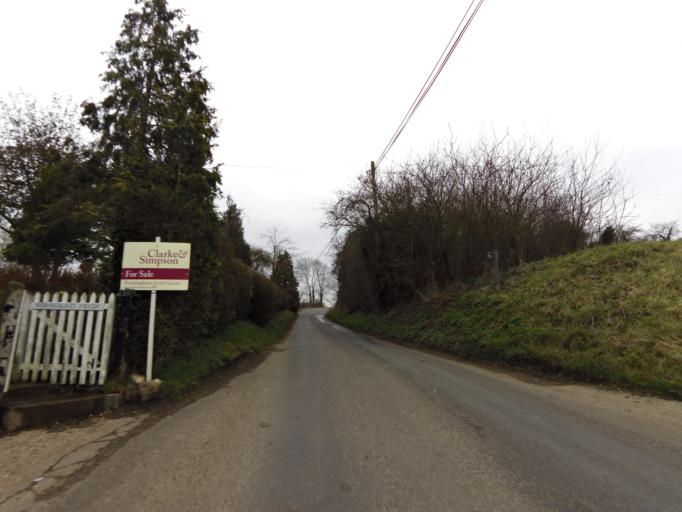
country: GB
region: England
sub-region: Suffolk
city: Framlingham
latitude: 52.2216
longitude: 1.3263
